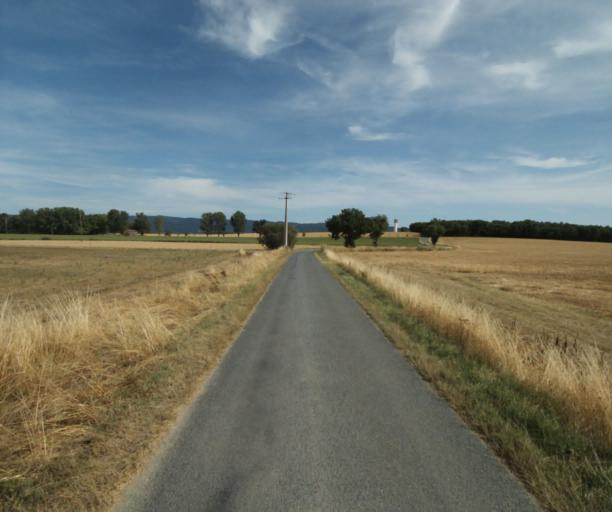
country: FR
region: Midi-Pyrenees
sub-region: Departement du Tarn
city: Soreze
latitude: 43.5097
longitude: 2.0446
